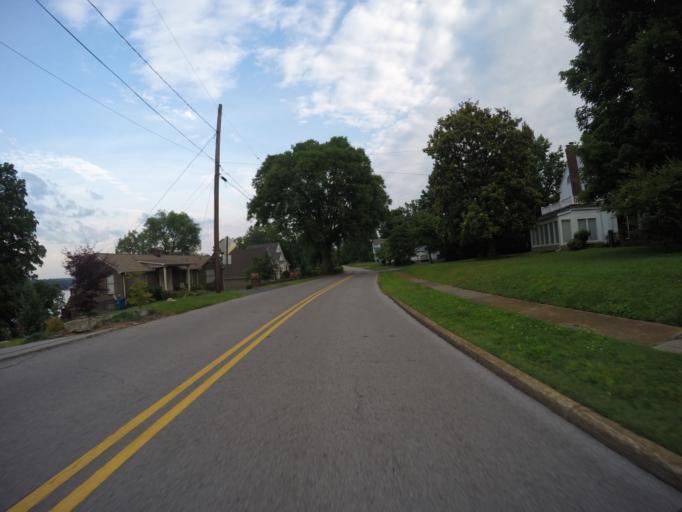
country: US
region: Tennessee
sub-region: Davidson County
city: Lakewood
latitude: 36.2623
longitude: -86.6442
